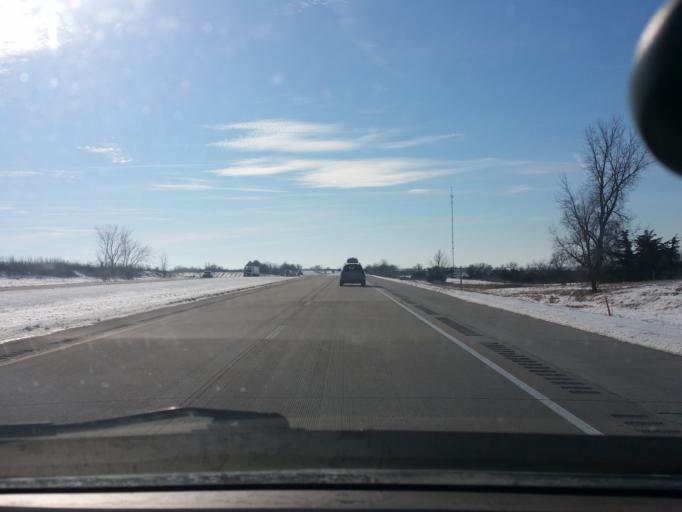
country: US
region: Iowa
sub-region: Decatur County
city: Leon
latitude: 40.7685
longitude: -93.8364
